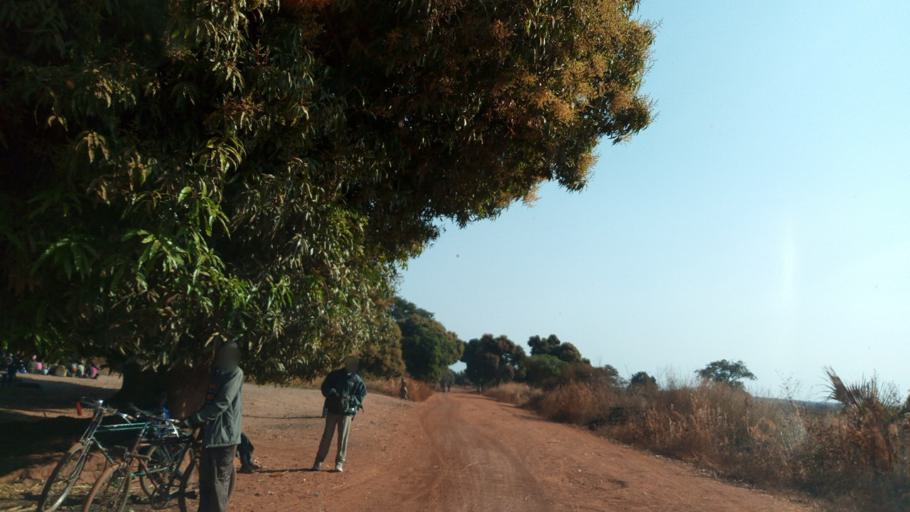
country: ZM
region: Luapula
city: Nchelenge
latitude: -9.2188
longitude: 28.2799
